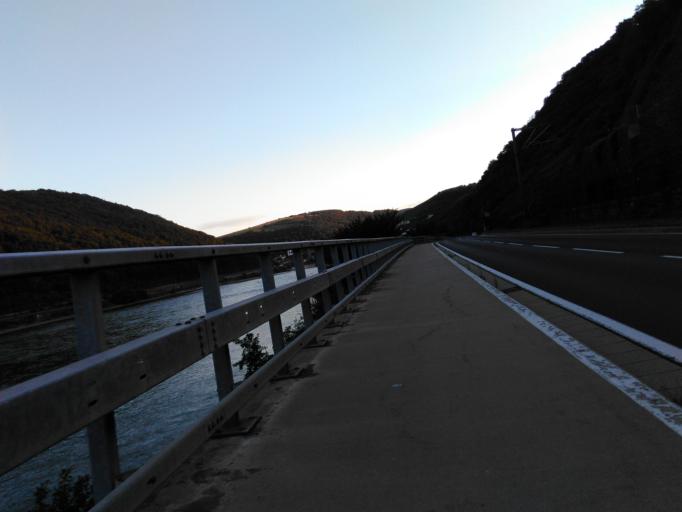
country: DE
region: Rheinland-Pfalz
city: Urbar
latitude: 50.1260
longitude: 7.7332
